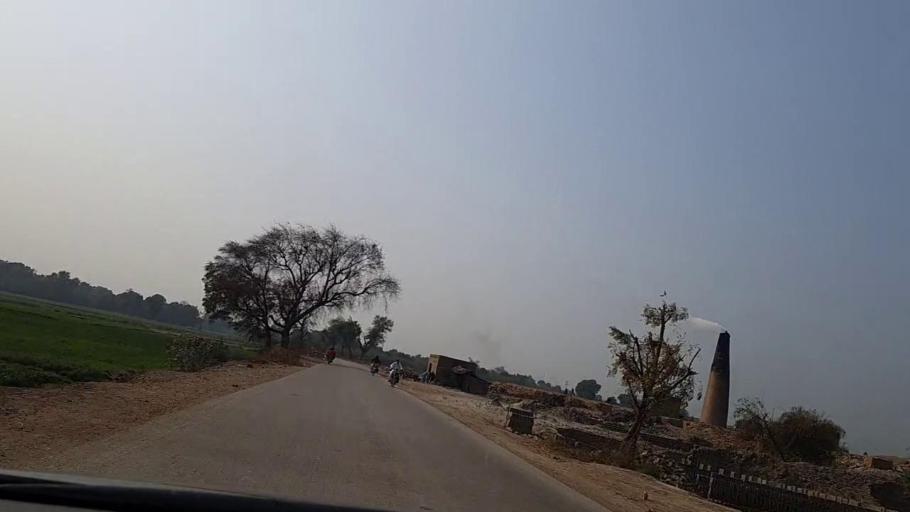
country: PK
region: Sindh
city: Sakrand
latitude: 26.1379
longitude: 68.2522
